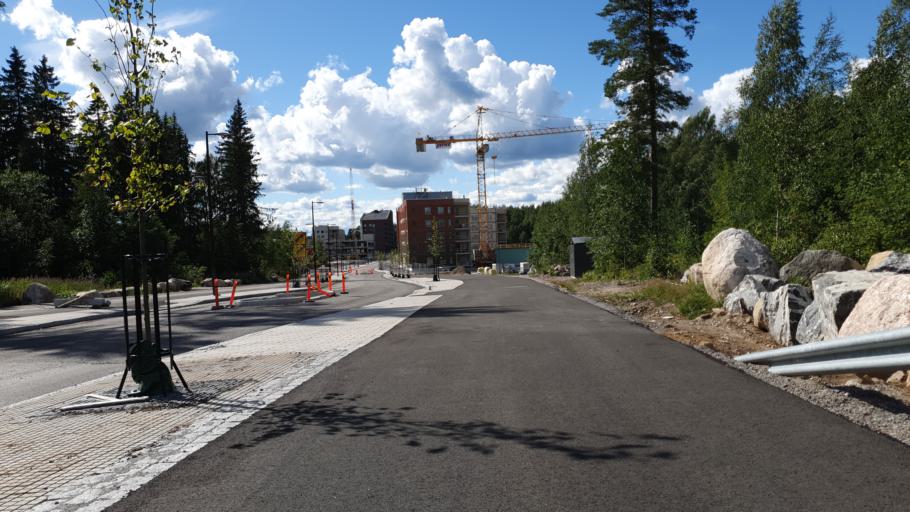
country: FI
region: Uusimaa
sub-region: Helsinki
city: Tuusula
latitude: 60.3986
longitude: 25.0428
